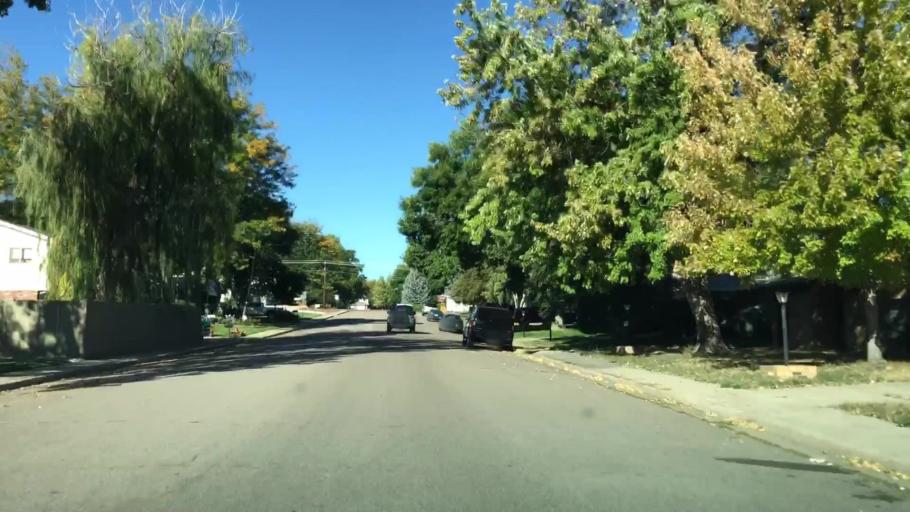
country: US
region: Colorado
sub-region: Larimer County
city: Loveland
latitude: 40.4142
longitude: -105.0569
